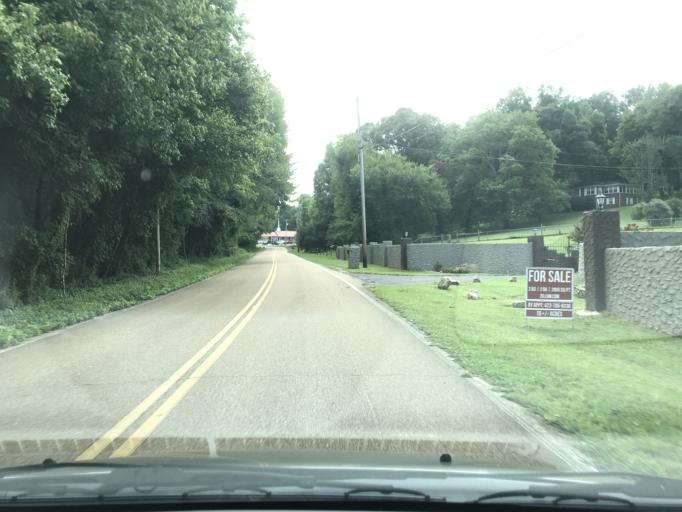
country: US
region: Tennessee
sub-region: Hamilton County
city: Lakesite
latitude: 35.2061
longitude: -85.0899
